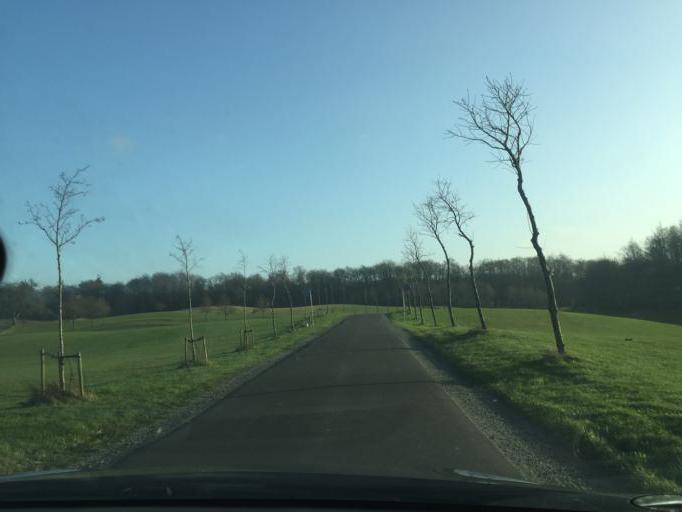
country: DK
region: South Denmark
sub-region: Faaborg-Midtfyn Kommune
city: Faaborg
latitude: 55.1355
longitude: 10.2549
